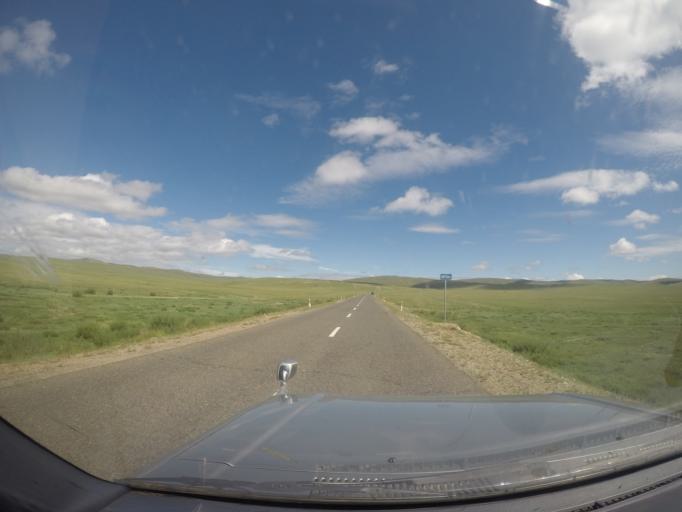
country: MN
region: Hentiy
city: Modot
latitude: 47.5962
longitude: 109.2491
